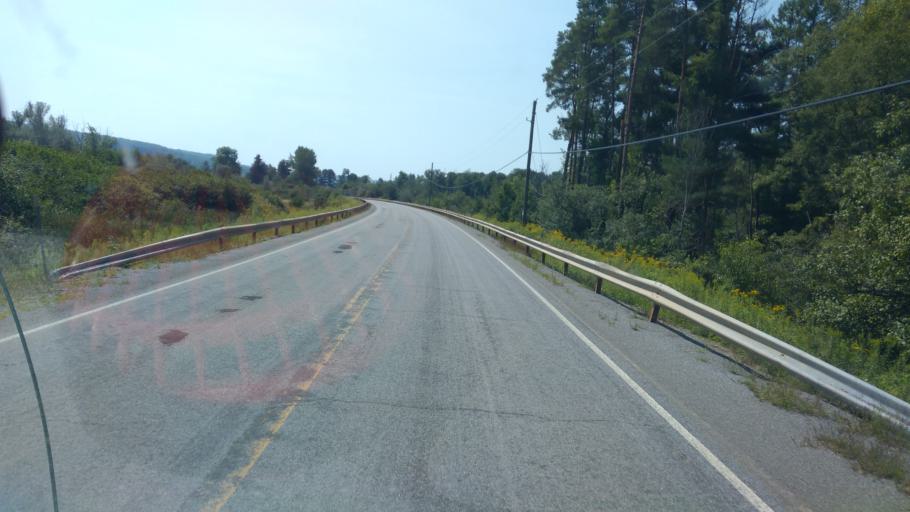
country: US
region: New York
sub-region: Allegany County
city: Alfred
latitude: 42.3487
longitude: -77.9253
